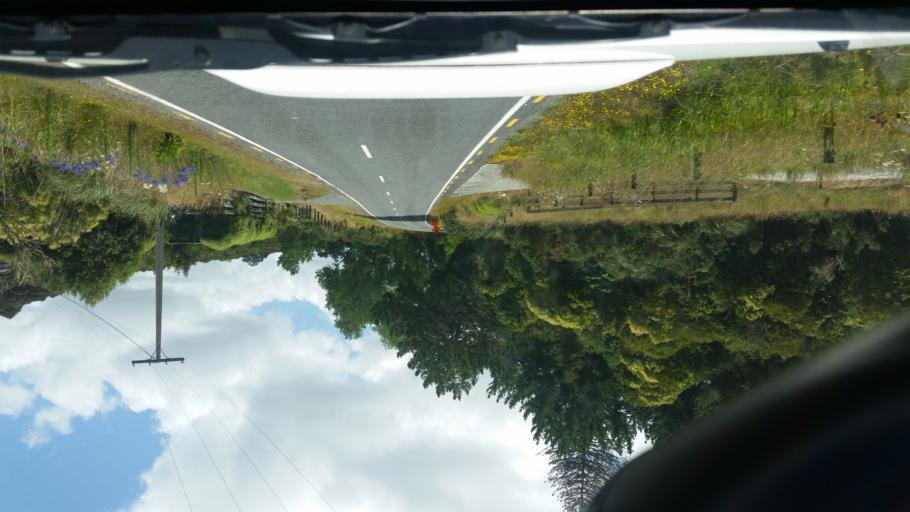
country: NZ
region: Northland
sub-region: Whangarei
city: Ruakaka
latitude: -36.0945
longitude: 174.2430
